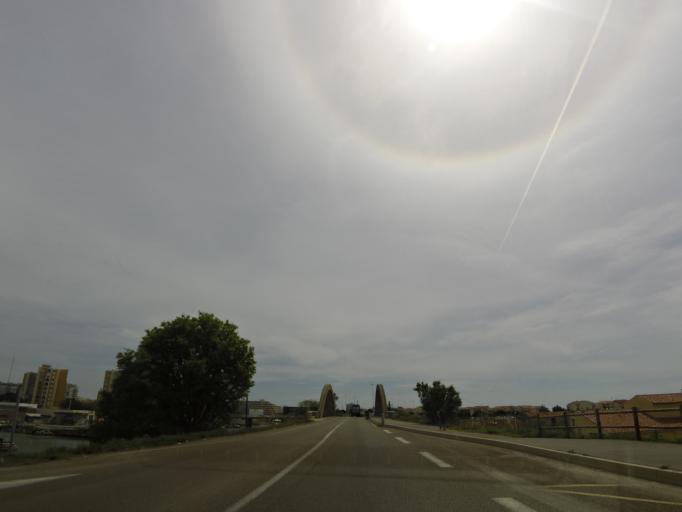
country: FR
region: Languedoc-Roussillon
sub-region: Departement de l'Herault
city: Perols
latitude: 43.5480
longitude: 3.9695
